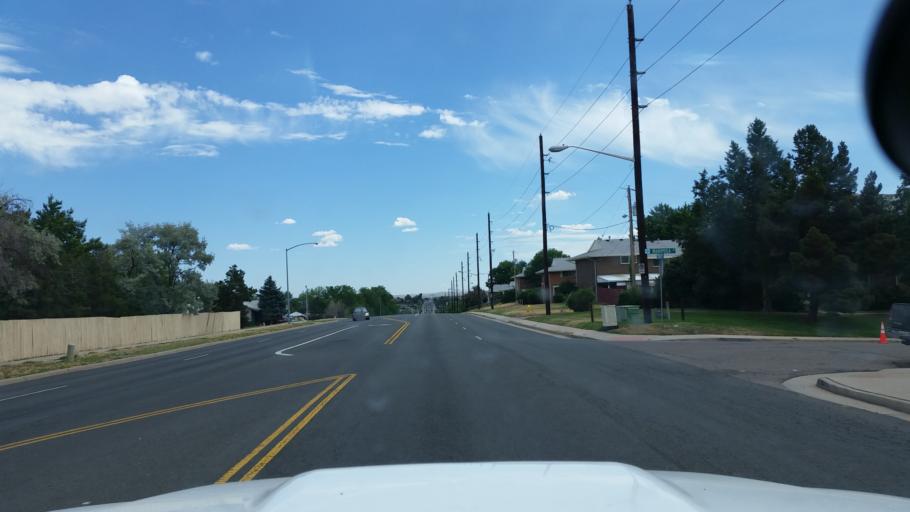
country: US
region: Colorado
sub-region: Adams County
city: Federal Heights
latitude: 39.8562
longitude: -105.0026
